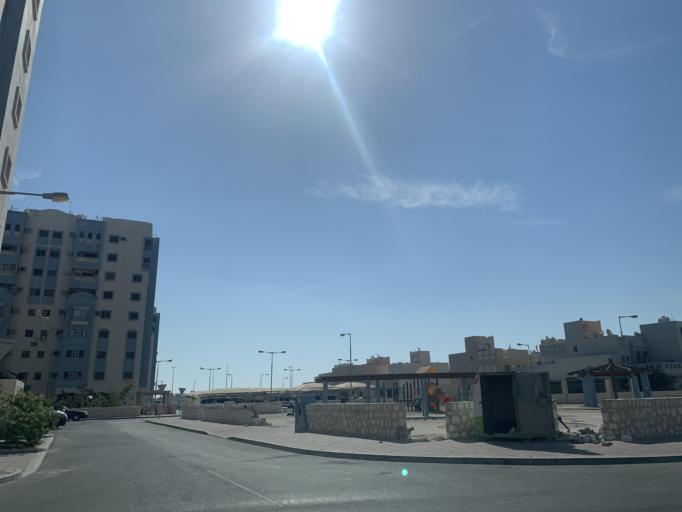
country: BH
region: Central Governorate
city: Madinat Hamad
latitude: 26.1148
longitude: 50.4906
